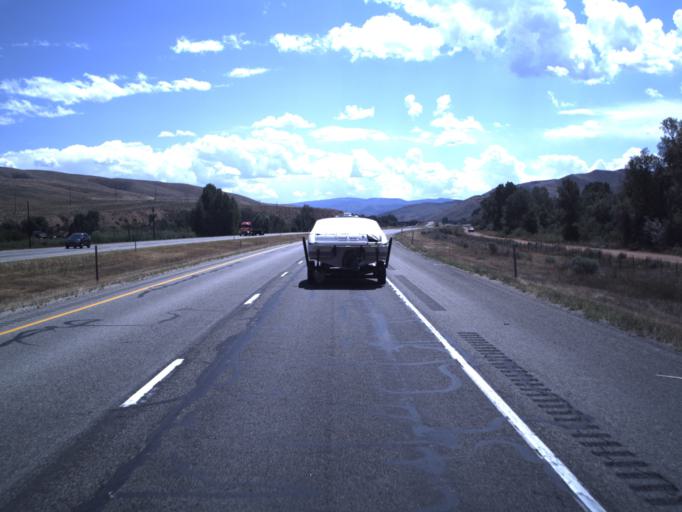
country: US
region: Utah
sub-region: Summit County
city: Coalville
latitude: 41.0288
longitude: -111.5009
